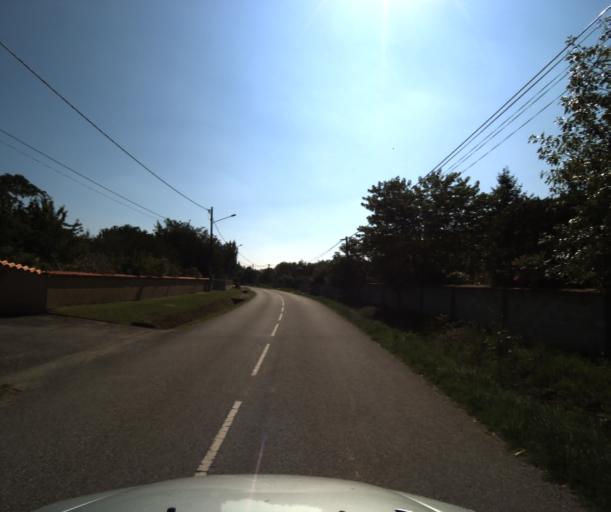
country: FR
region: Midi-Pyrenees
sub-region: Departement de la Haute-Garonne
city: Lacasse
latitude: 43.3905
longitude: 1.2515
